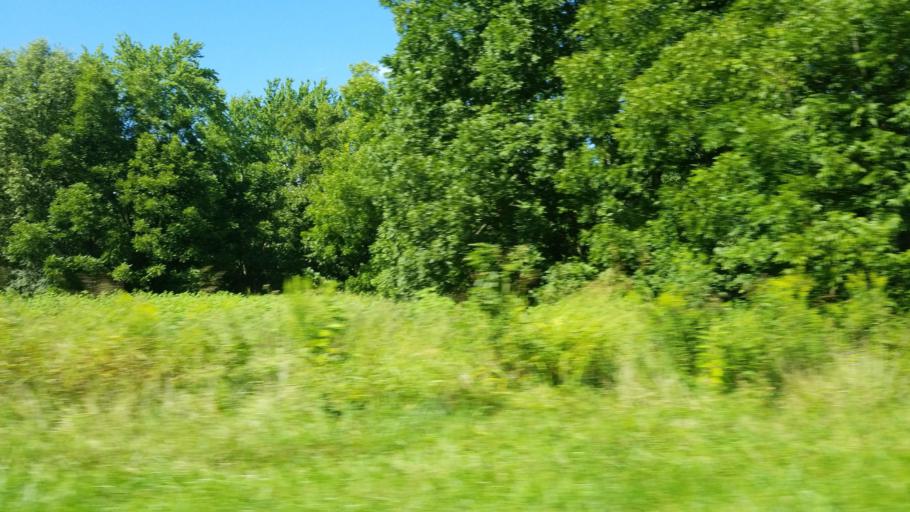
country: US
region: Illinois
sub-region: Williamson County
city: Marion
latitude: 37.7445
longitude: -88.8848
